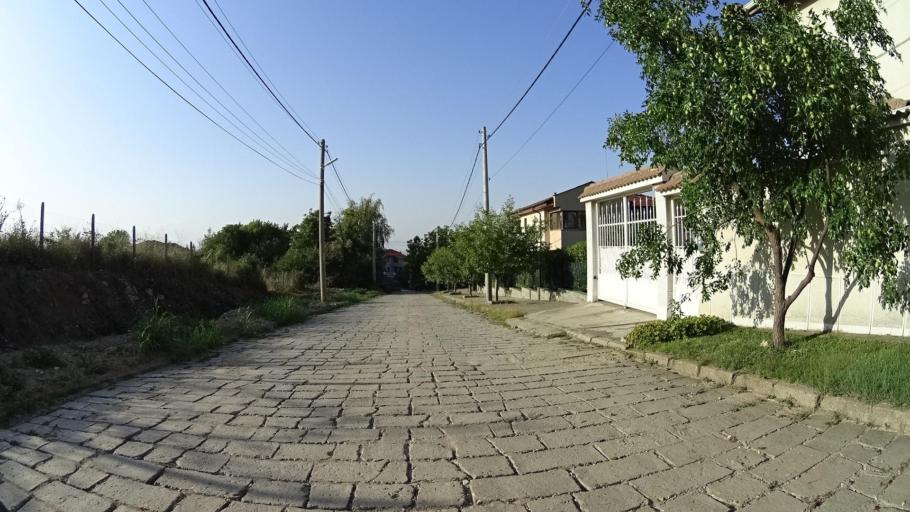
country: BG
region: Plovdiv
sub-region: Obshtina Plovdiv
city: Plovdiv
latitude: 42.0630
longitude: 24.6994
